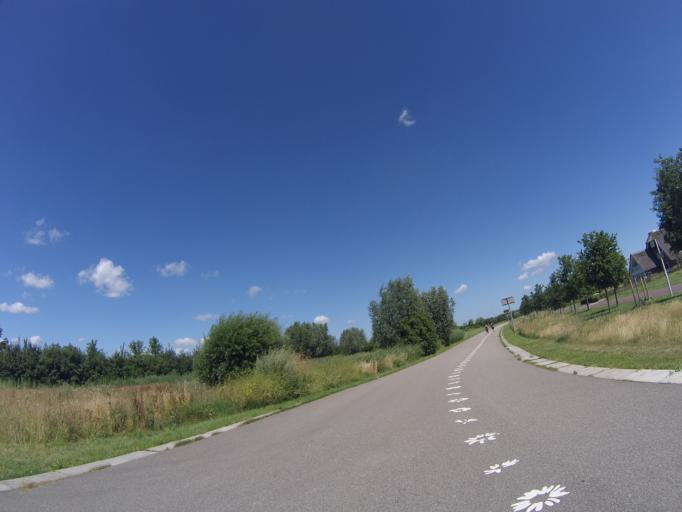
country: NL
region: Utrecht
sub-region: Stichtse Vecht
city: Spechtenkamp
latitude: 52.1066
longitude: 5.0293
